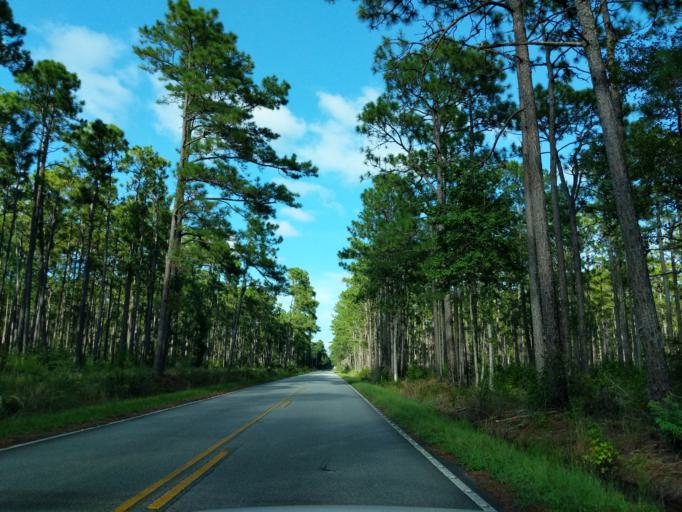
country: US
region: South Carolina
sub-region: Charleston County
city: Awendaw
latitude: 33.1367
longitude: -79.4314
